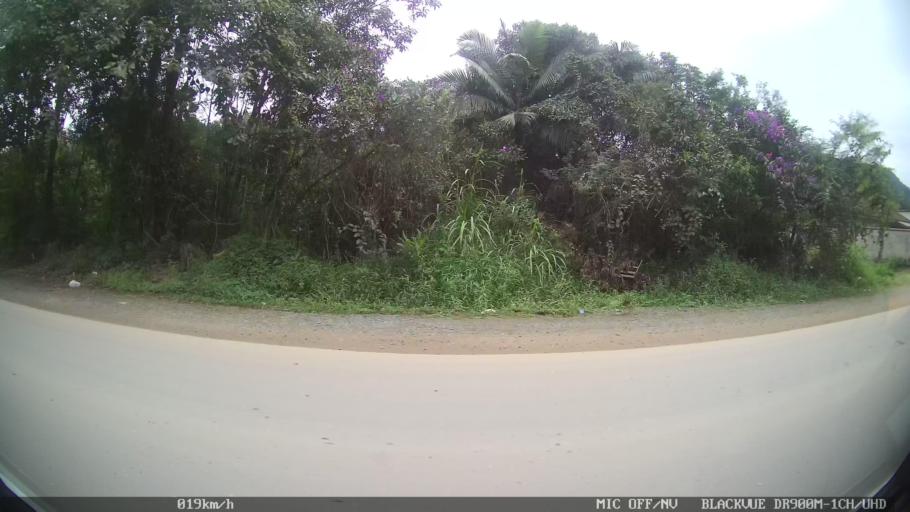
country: BR
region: Santa Catarina
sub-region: Joinville
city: Joinville
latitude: -26.2566
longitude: -48.9249
